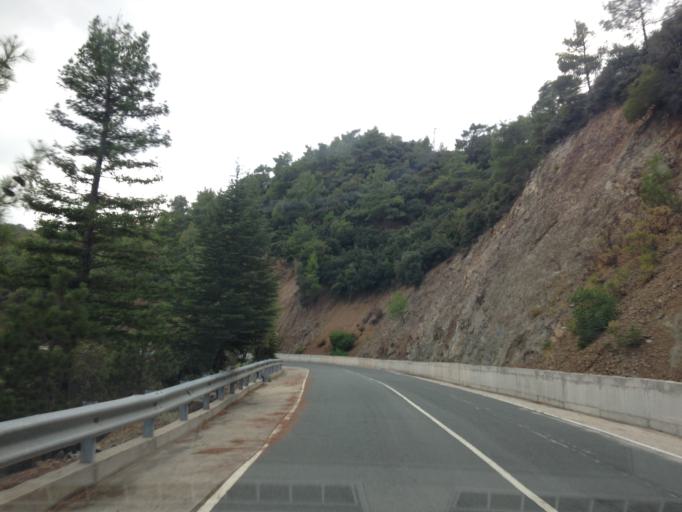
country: CY
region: Lefkosia
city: Lefka
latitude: 34.9930
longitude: 32.7378
